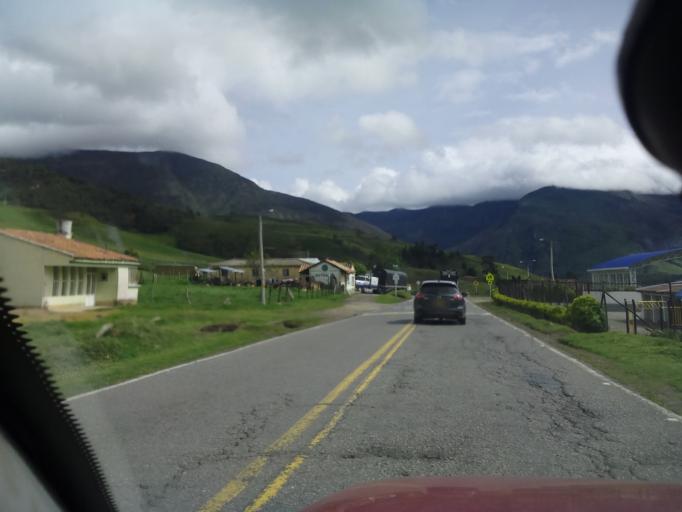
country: CO
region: Boyaca
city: Combita
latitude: 5.6906
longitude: -73.3673
